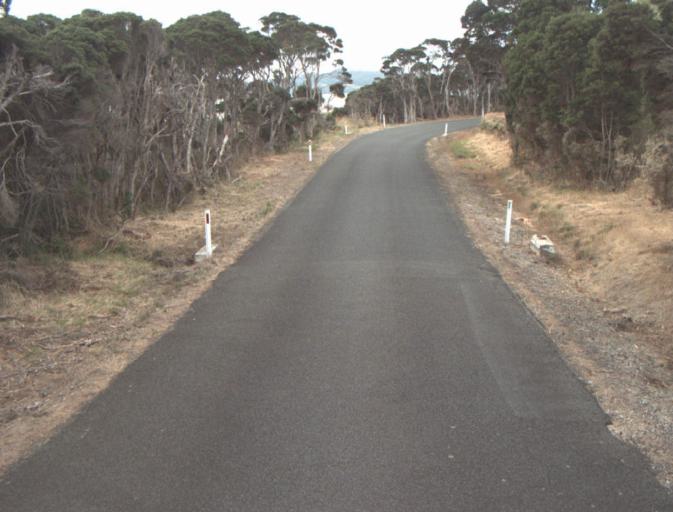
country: AU
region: Tasmania
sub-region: Launceston
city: Mayfield
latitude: -41.2908
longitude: 146.9908
